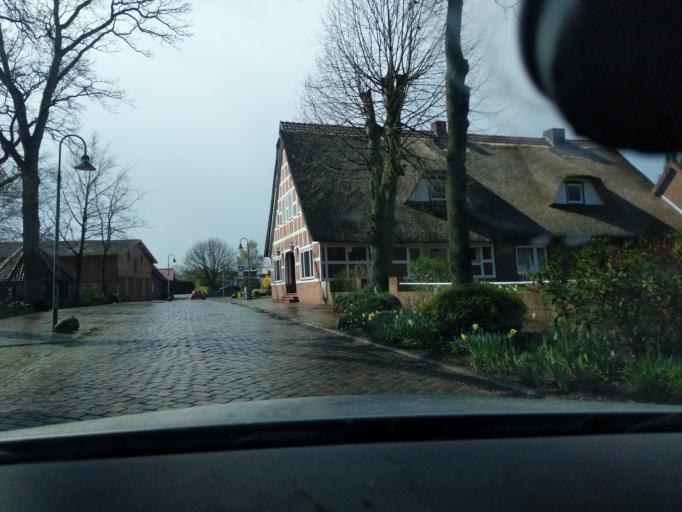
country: DE
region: Lower Saxony
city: Bargstedt
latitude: 53.4597
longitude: 9.4473
